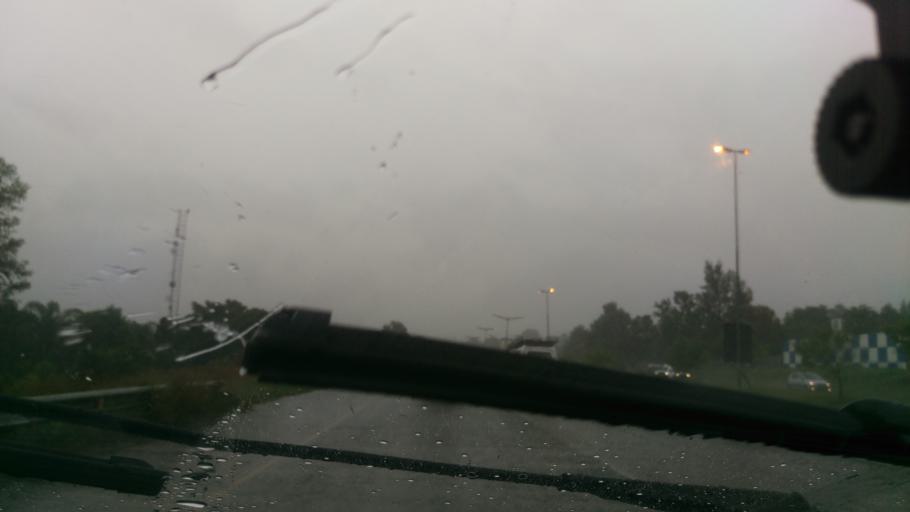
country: ZA
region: Gauteng
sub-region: West Rand District Municipality
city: Muldersdriseloop
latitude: -26.0740
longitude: 27.9362
